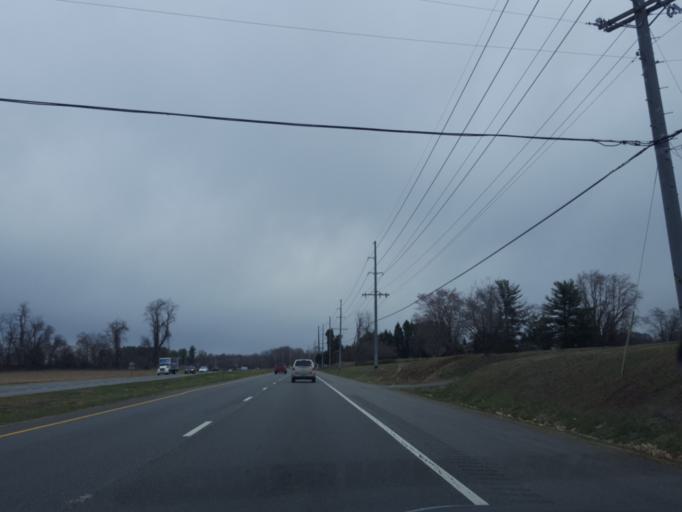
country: US
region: Maryland
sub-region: Calvert County
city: Dunkirk
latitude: 38.7297
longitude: -76.6592
